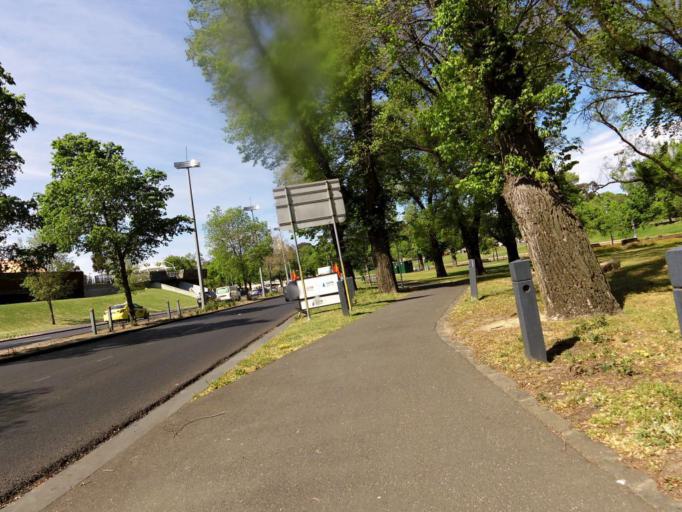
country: AU
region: Victoria
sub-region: Melbourne
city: Southbank
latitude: -37.8200
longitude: 144.9761
